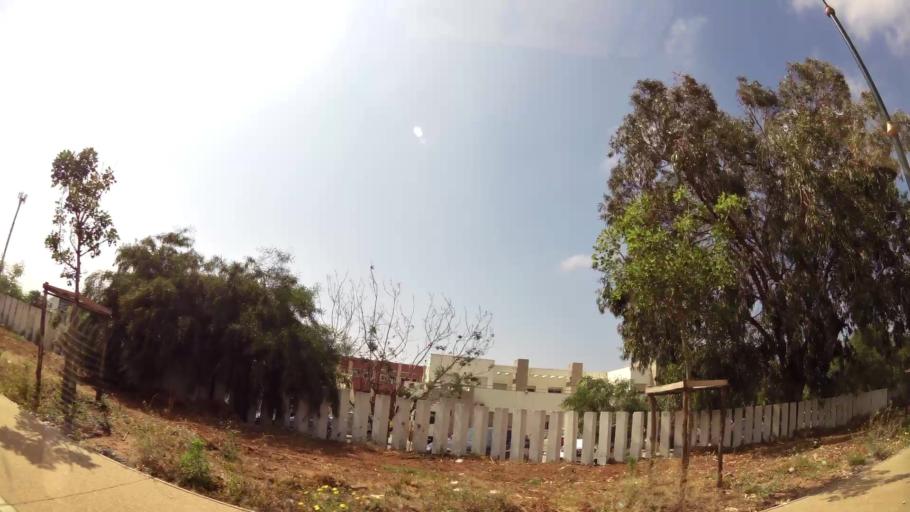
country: MA
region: Rabat-Sale-Zemmour-Zaer
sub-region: Rabat
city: Rabat
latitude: 33.9783
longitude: -6.8608
